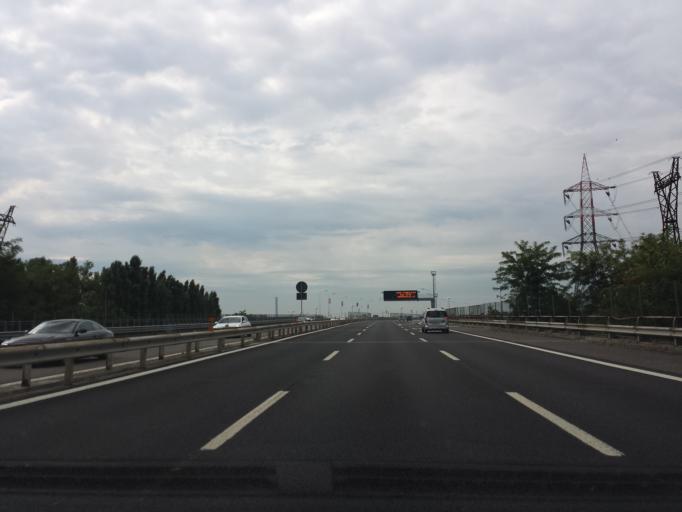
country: IT
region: Lombardy
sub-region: Citta metropolitana di Milano
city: Rho
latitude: 45.5287
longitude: 9.0609
